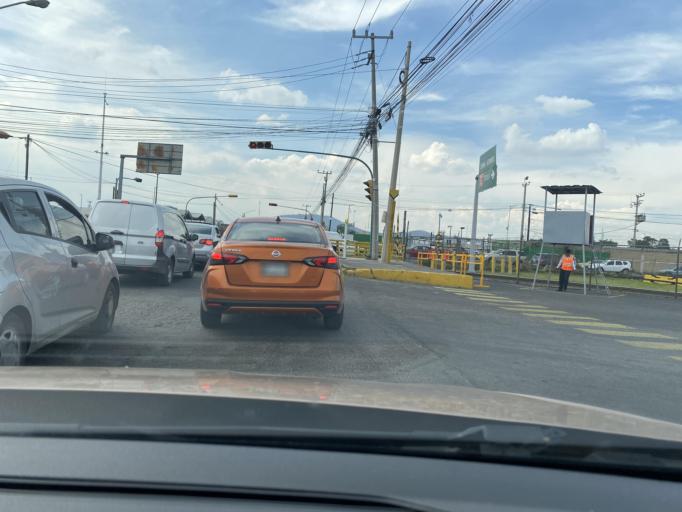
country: IN
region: Karnataka
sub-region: Dakshina Kannada
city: Puttur
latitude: 12.7414
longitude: 75.1903
